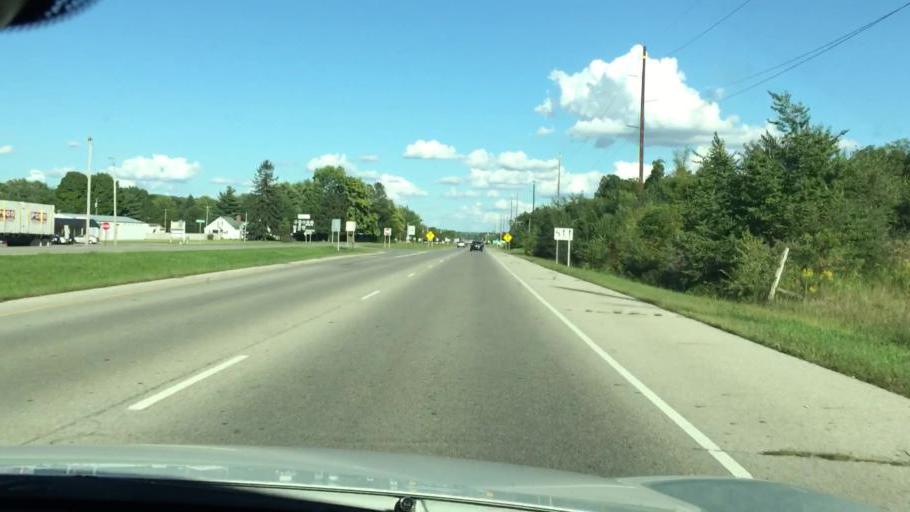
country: US
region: Ohio
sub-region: Clark County
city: Springfield
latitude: 39.9229
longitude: -83.7432
